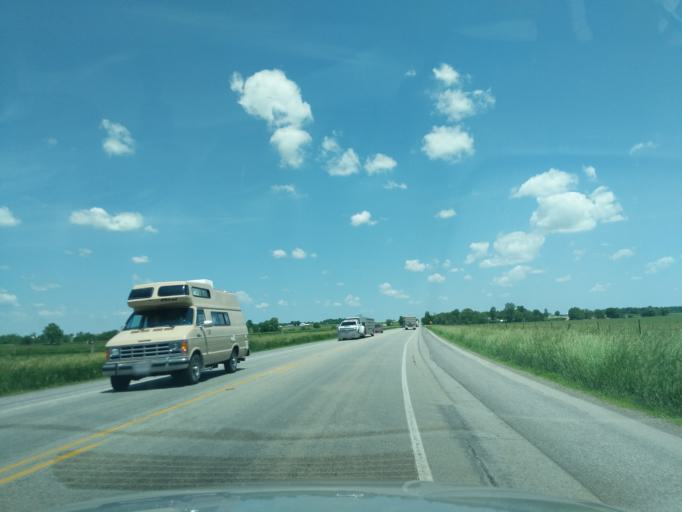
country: US
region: Indiana
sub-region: LaGrange County
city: Topeka
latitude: 41.6121
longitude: -85.5795
